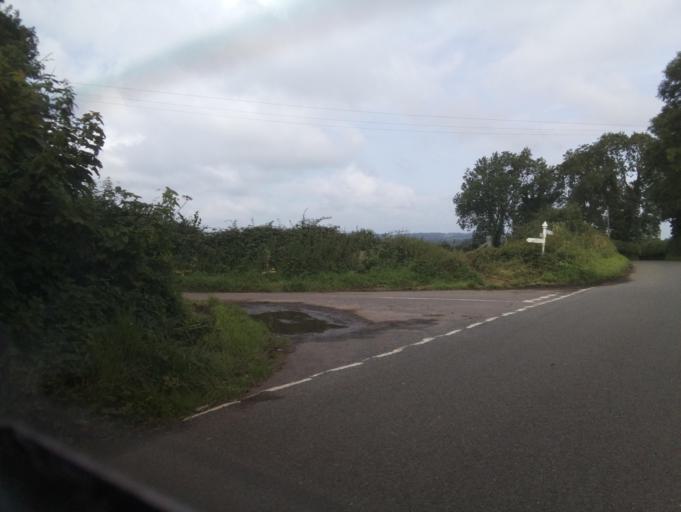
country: GB
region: England
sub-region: Bath and North East Somerset
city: Cameley
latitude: 51.2626
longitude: -2.5685
